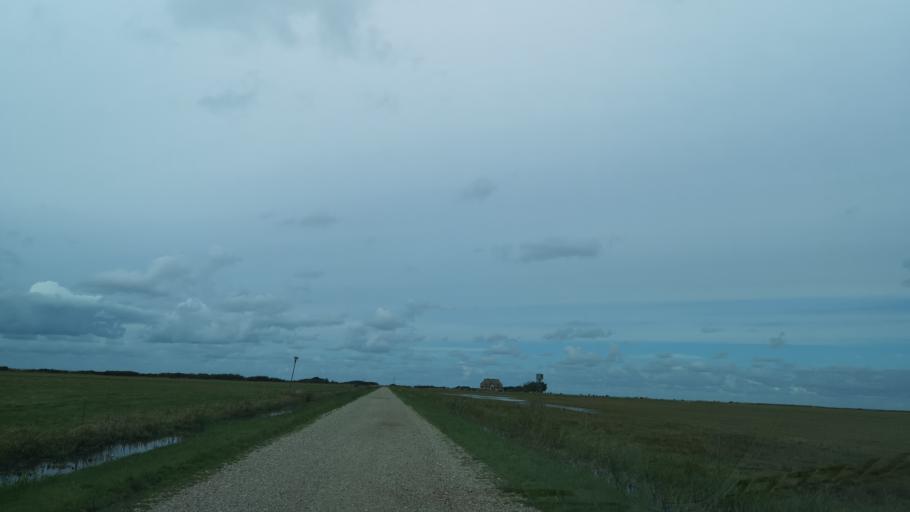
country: DK
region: Central Jutland
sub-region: Ringkobing-Skjern Kommune
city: Hvide Sande
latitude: 55.8918
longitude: 8.2152
